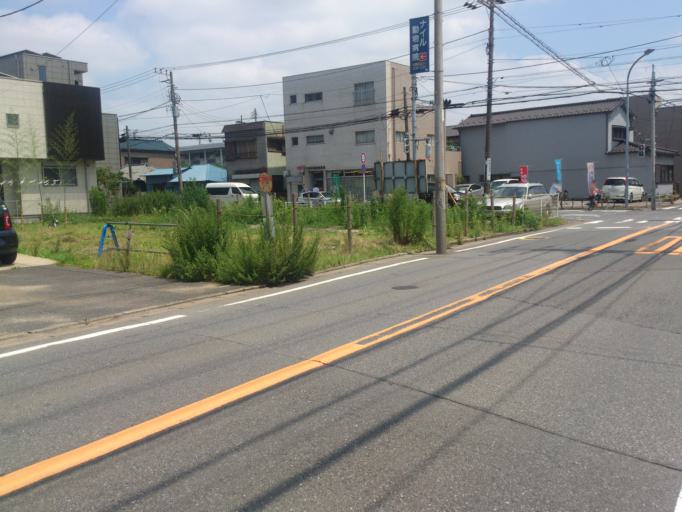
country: JP
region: Chiba
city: Chiba
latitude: 35.5958
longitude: 140.1204
